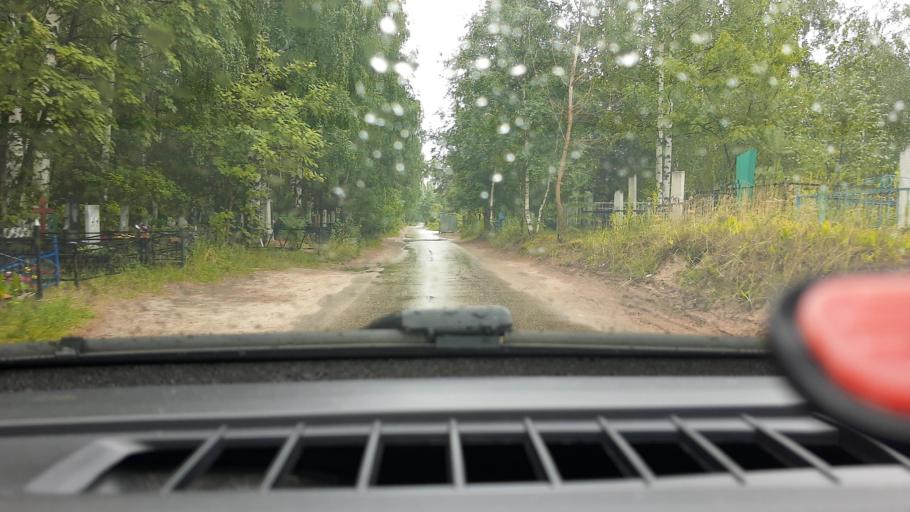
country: RU
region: Nizjnij Novgorod
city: Gorbatovka
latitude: 56.3553
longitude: 43.7776
